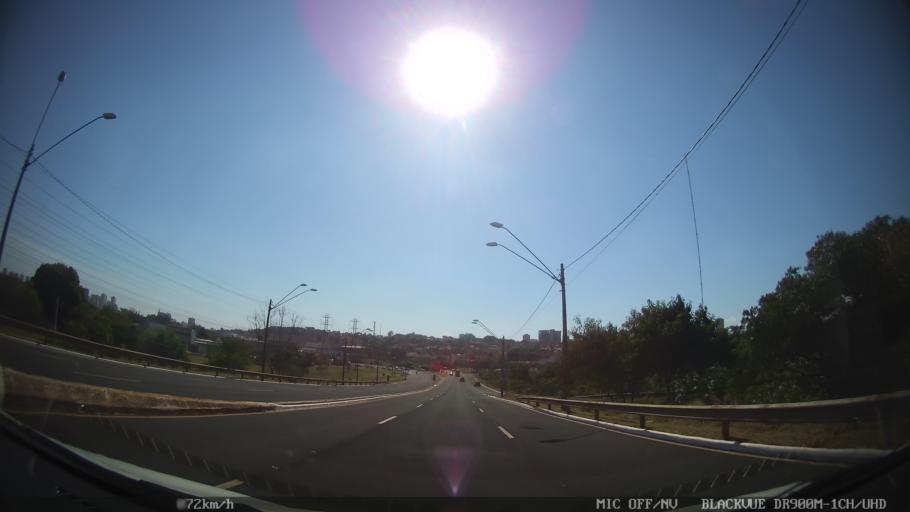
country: BR
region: Sao Paulo
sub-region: Ribeirao Preto
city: Ribeirao Preto
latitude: -21.2144
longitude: -47.7732
